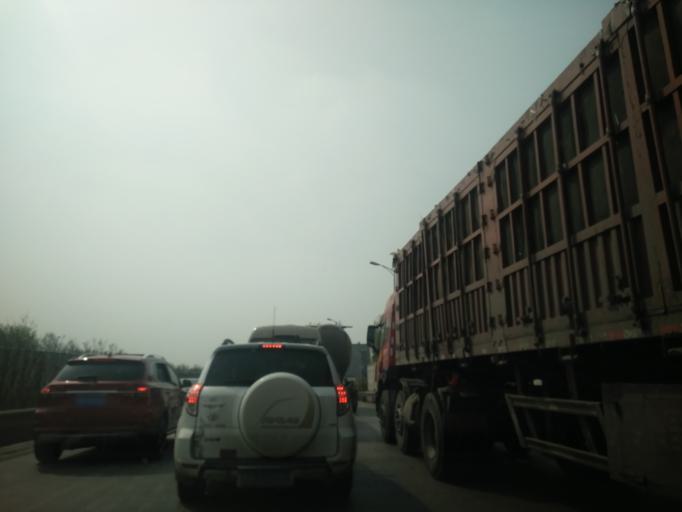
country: CN
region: Beijing
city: Xiji
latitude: 39.7990
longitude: 116.9005
